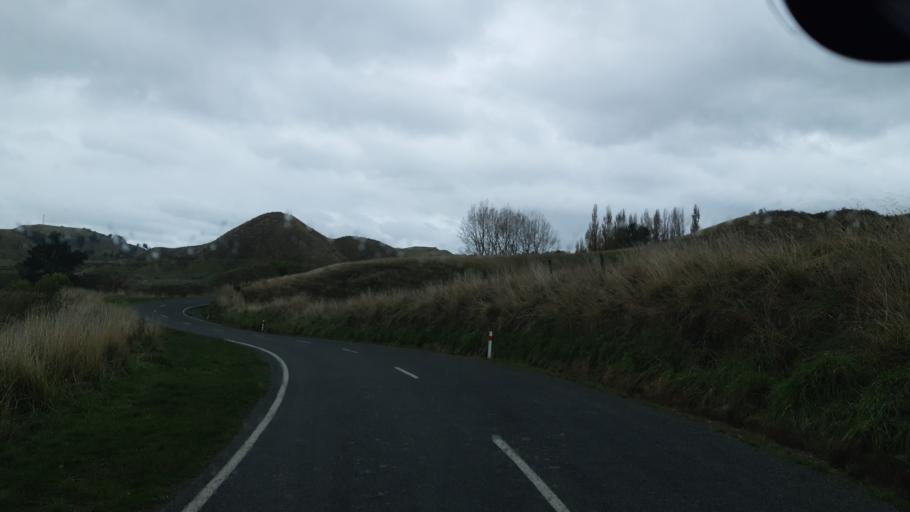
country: NZ
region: Manawatu-Wanganui
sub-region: Ruapehu District
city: Waiouru
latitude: -39.6117
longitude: 175.6112
